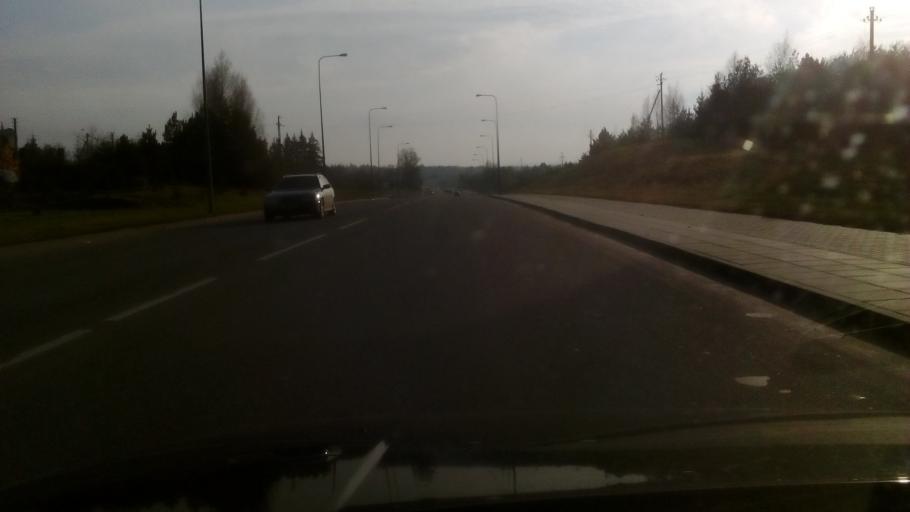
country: LT
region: Alytaus apskritis
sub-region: Alytus
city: Alytus
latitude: 54.3952
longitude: 23.9991
